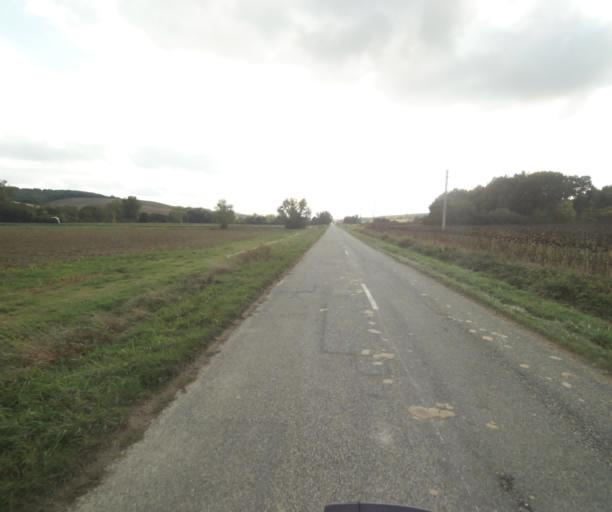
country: FR
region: Midi-Pyrenees
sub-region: Departement de la Haute-Garonne
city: Launac
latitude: 43.8097
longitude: 1.1145
